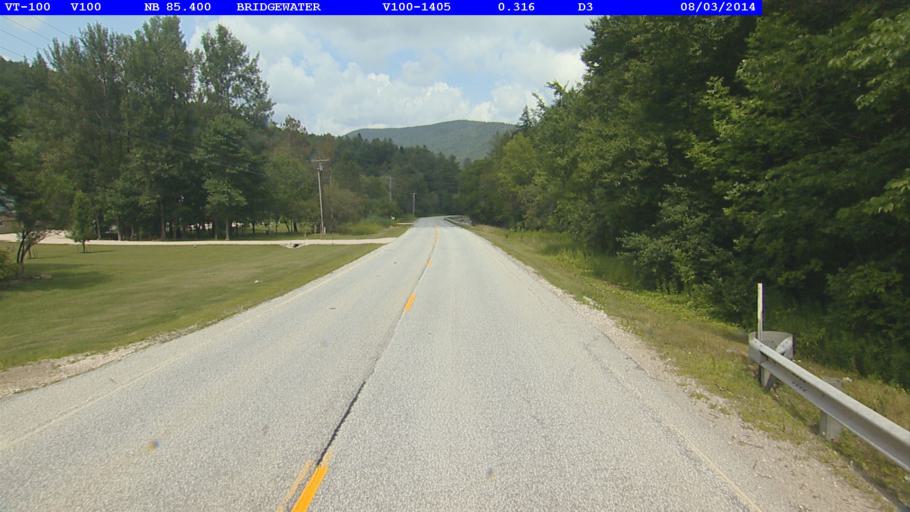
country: US
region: Vermont
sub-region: Rutland County
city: Rutland
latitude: 43.5914
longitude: -72.7541
